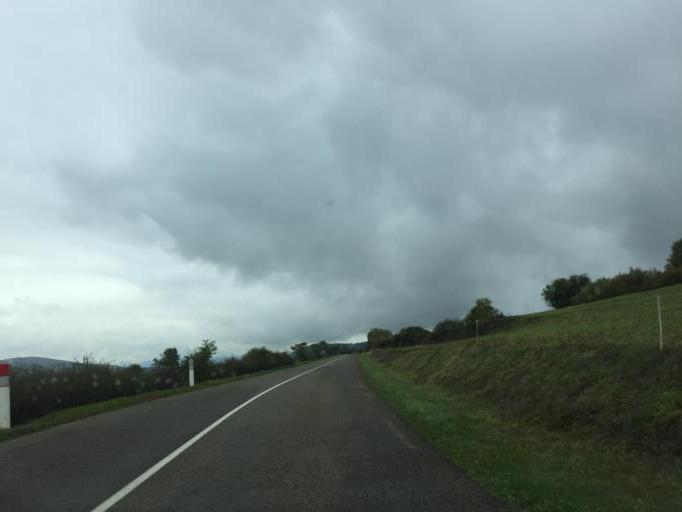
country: FR
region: Franche-Comte
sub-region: Departement du Jura
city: Orgelet
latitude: 46.5109
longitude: 5.6060
